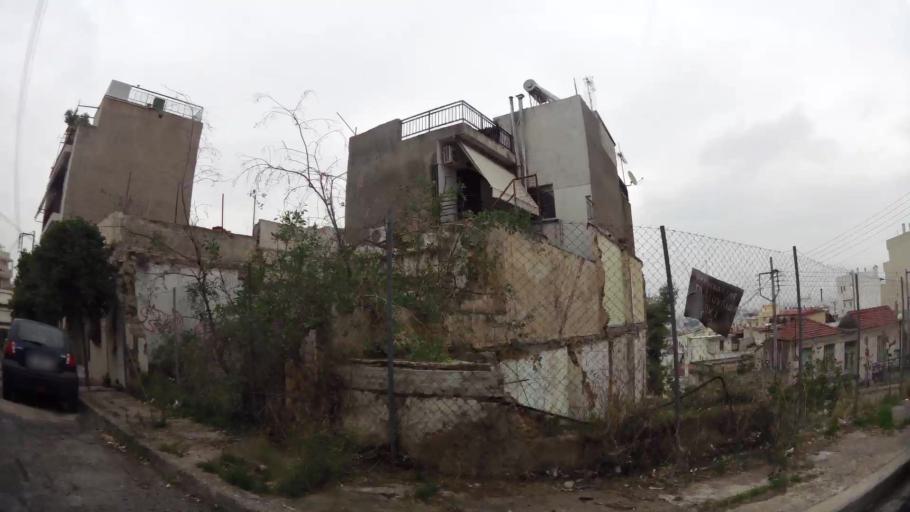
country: GR
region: Attica
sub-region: Nomos Piraios
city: Nikaia
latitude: 37.9598
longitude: 23.6459
